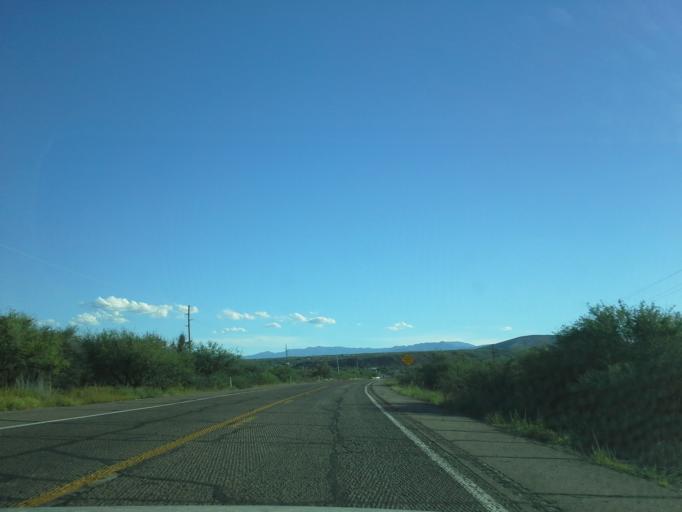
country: US
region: Arizona
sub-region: Pinal County
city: Mammoth
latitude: 32.7473
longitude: -110.6465
